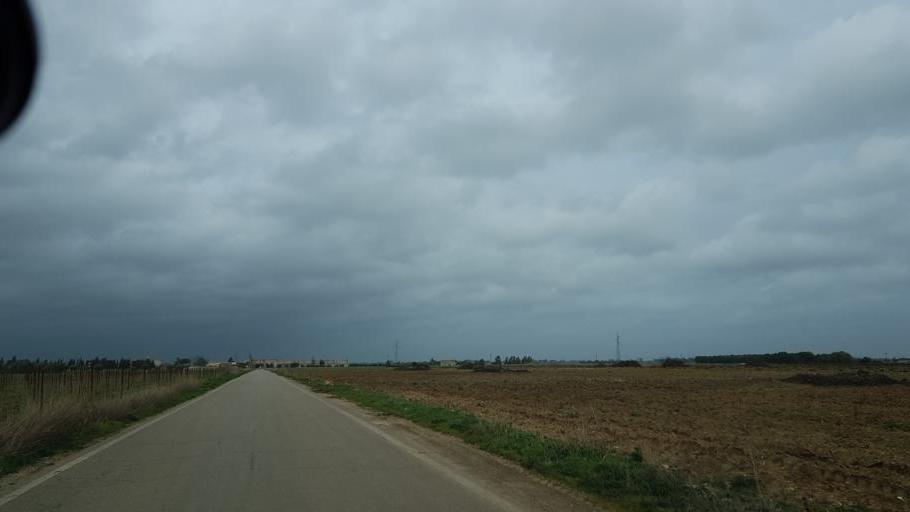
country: IT
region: Apulia
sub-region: Provincia di Brindisi
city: Brindisi
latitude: 40.6026
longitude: 17.8929
